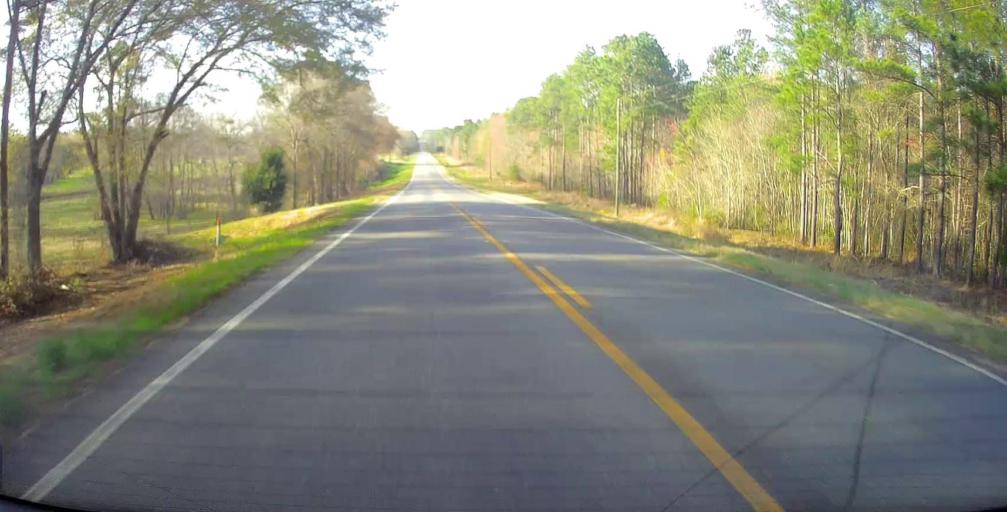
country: US
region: Georgia
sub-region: Toombs County
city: Lyons
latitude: 32.1606
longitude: -82.2694
